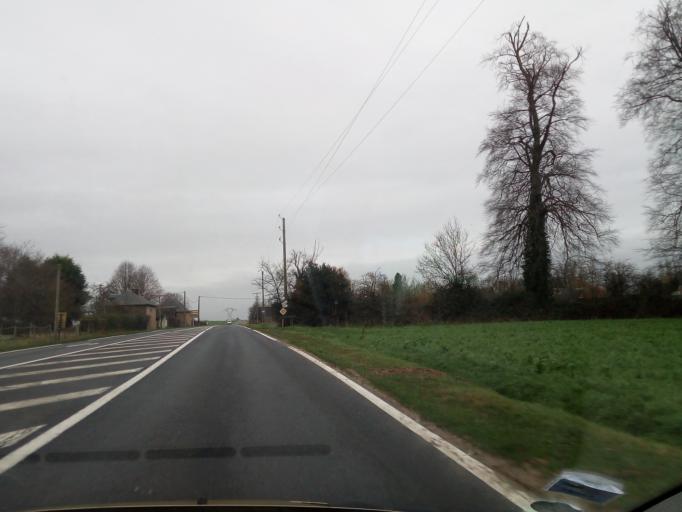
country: FR
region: Haute-Normandie
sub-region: Departement de l'Eure
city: Hauville
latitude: 49.3891
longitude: 0.7986
